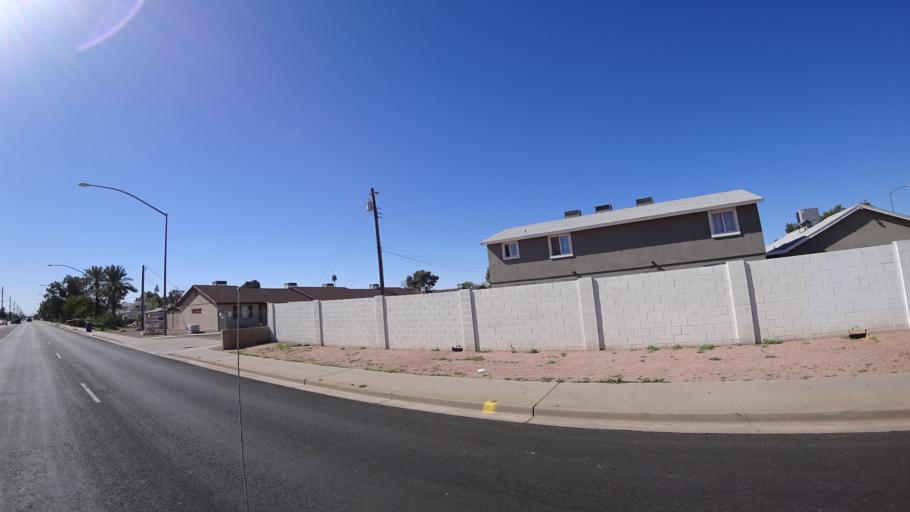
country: US
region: Arizona
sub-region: Maricopa County
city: Mesa
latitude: 33.4060
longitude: -111.8054
